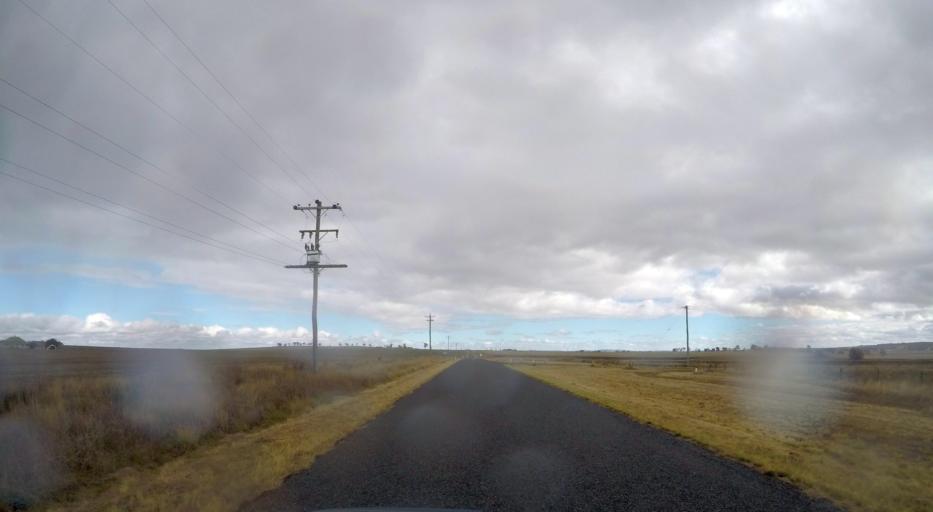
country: AU
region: Queensland
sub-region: Southern Downs
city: Warwick
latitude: -28.0539
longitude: 152.0265
